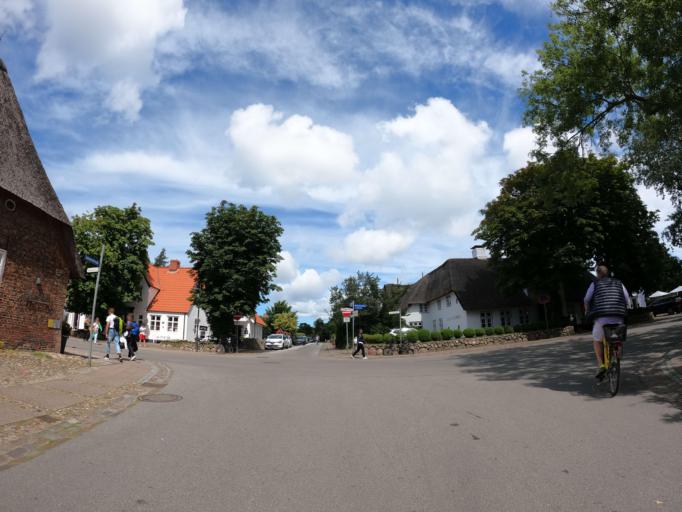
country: DE
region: Schleswig-Holstein
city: Keitum
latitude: 54.8940
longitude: 8.3699
